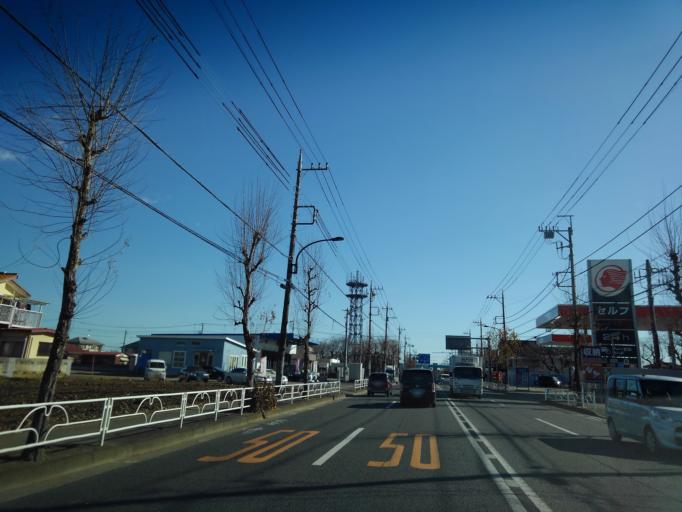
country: JP
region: Tokyo
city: Fussa
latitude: 35.7569
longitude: 139.3710
